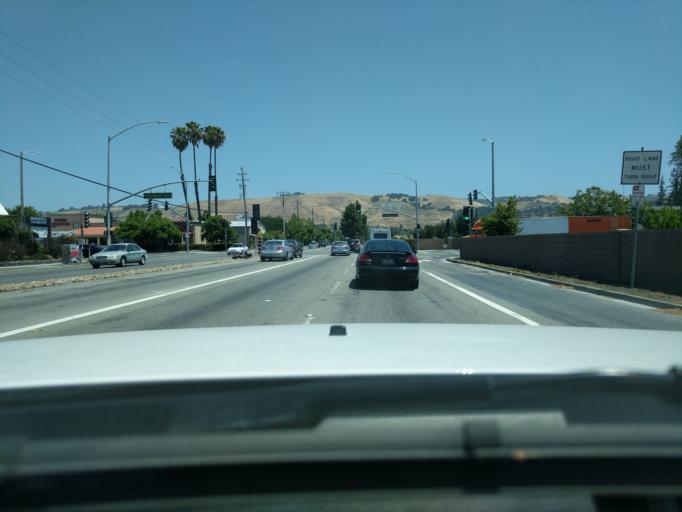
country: US
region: California
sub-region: Alameda County
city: Union City
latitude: 37.6213
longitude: -122.0574
